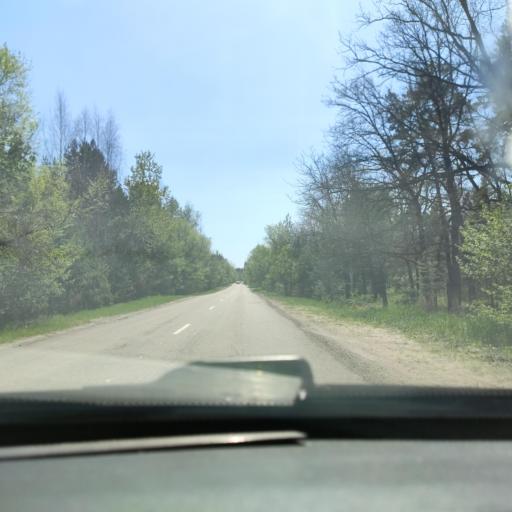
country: RU
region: Voronezj
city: Somovo
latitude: 51.7222
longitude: 39.3669
